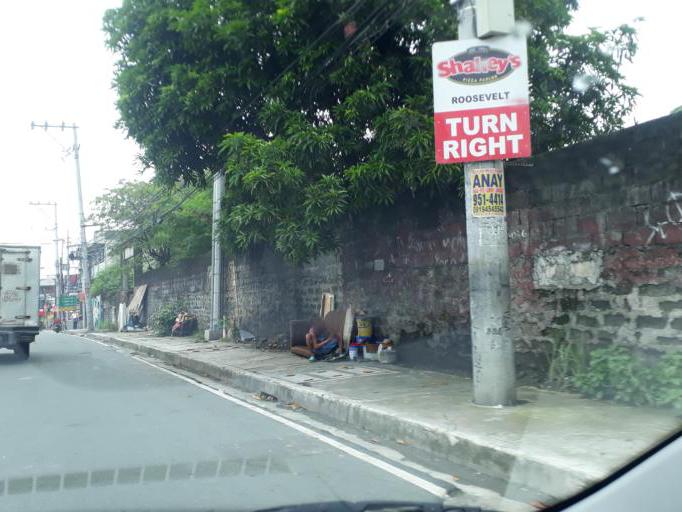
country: PH
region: Calabarzon
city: Del Monte
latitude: 14.6433
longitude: 121.0168
